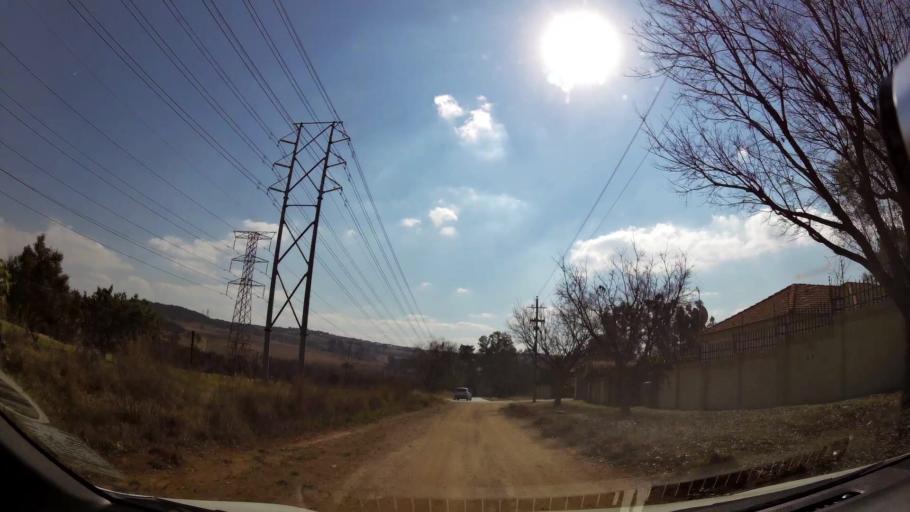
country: ZA
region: Gauteng
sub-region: City of Johannesburg Metropolitan Municipality
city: Midrand
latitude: -26.0100
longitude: 28.0707
